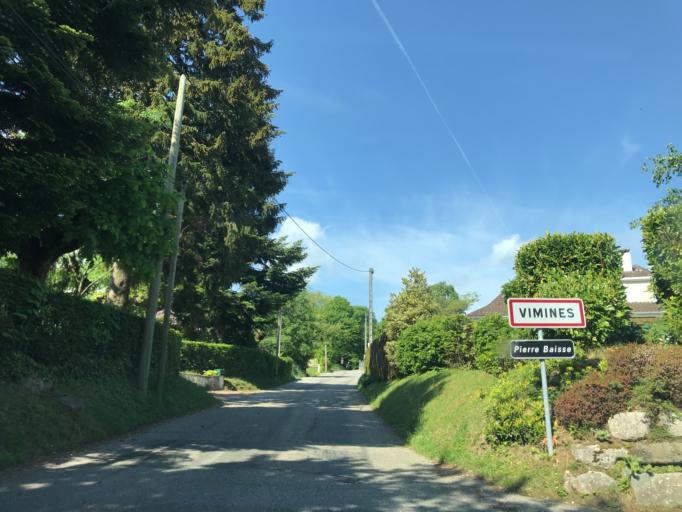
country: FR
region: Rhone-Alpes
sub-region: Departement de la Savoie
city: Vimines
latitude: 45.5491
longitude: 5.8700
